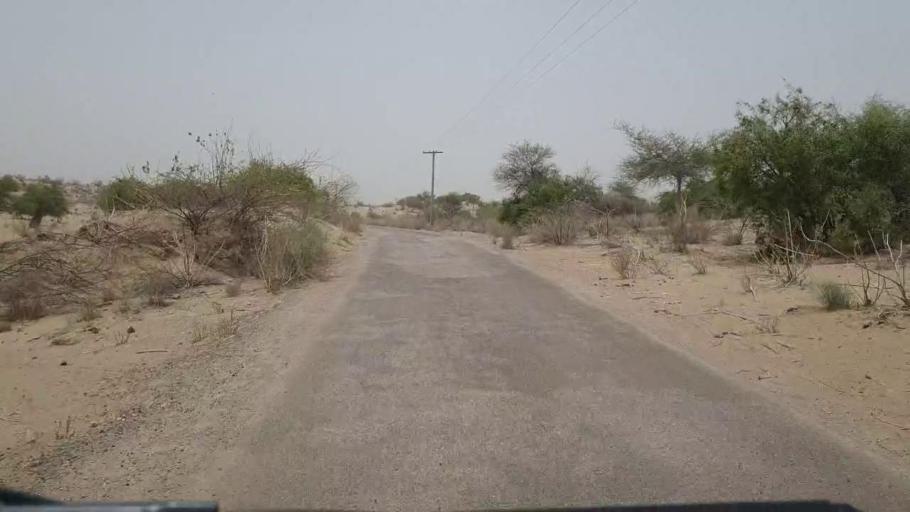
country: PK
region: Sindh
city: Naukot
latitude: 24.7482
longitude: 69.5507
